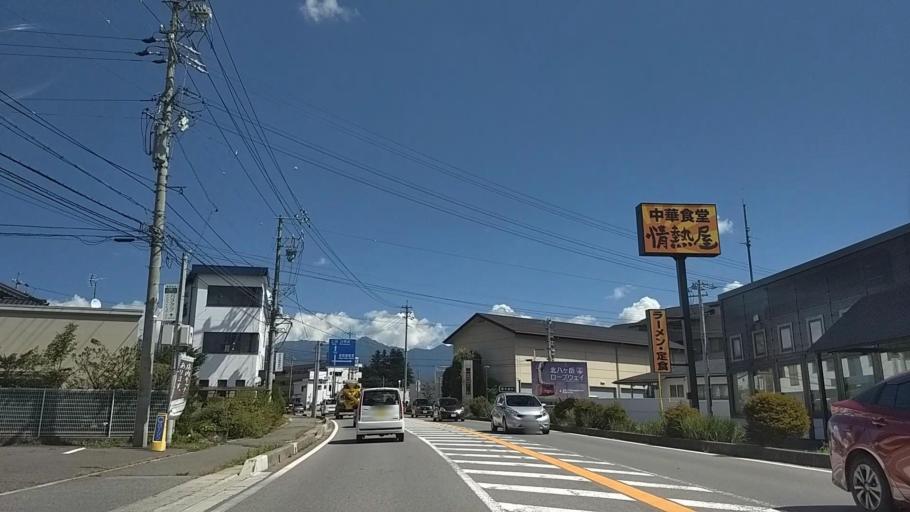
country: JP
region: Nagano
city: Chino
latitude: 35.9982
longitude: 138.1608
